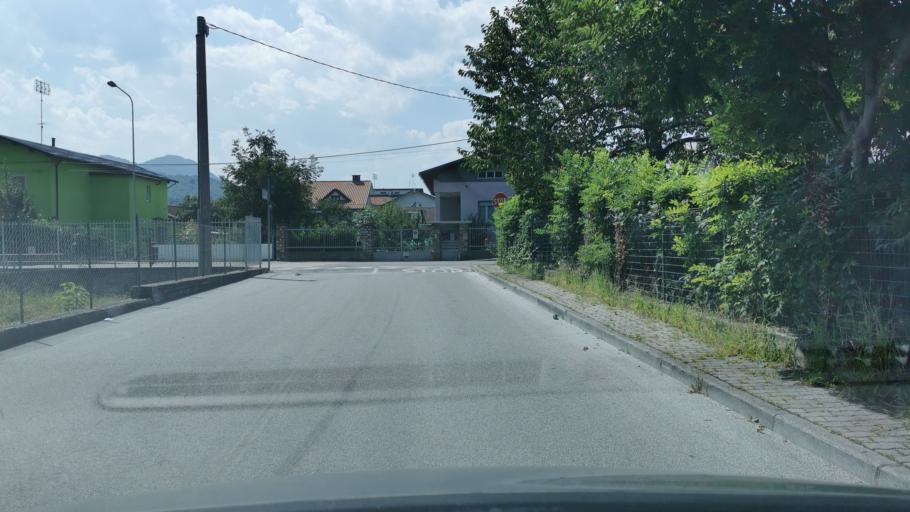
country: IT
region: Piedmont
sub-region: Provincia di Cuneo
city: Borgo San Dalmazzo
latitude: 44.3345
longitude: 7.4888
